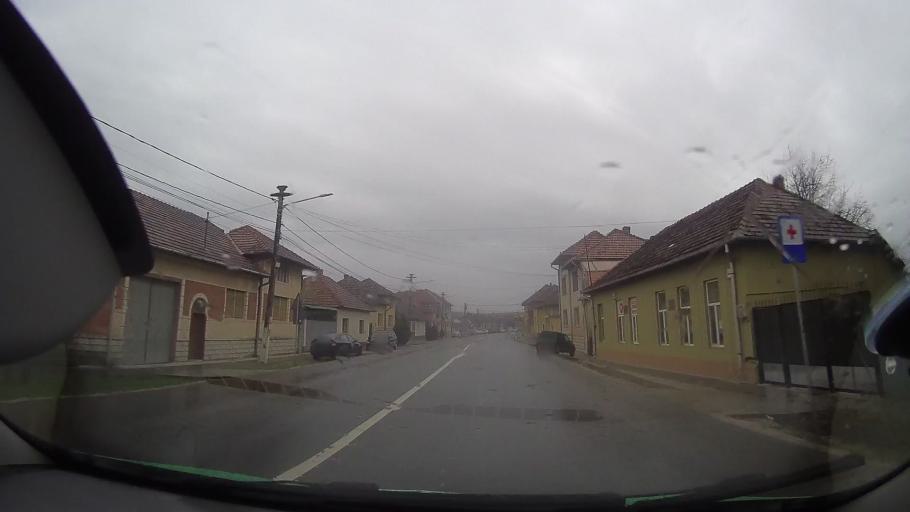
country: RO
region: Bihor
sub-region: Comuna Pocola
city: Pocola
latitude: 46.6953
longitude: 22.2921
